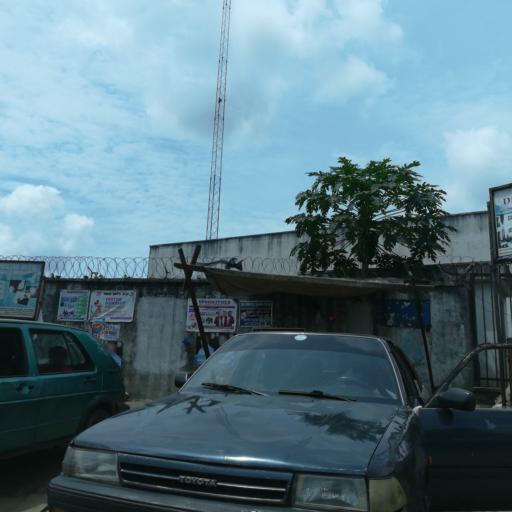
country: NG
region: Rivers
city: Port Harcourt
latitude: 4.7826
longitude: 7.0402
